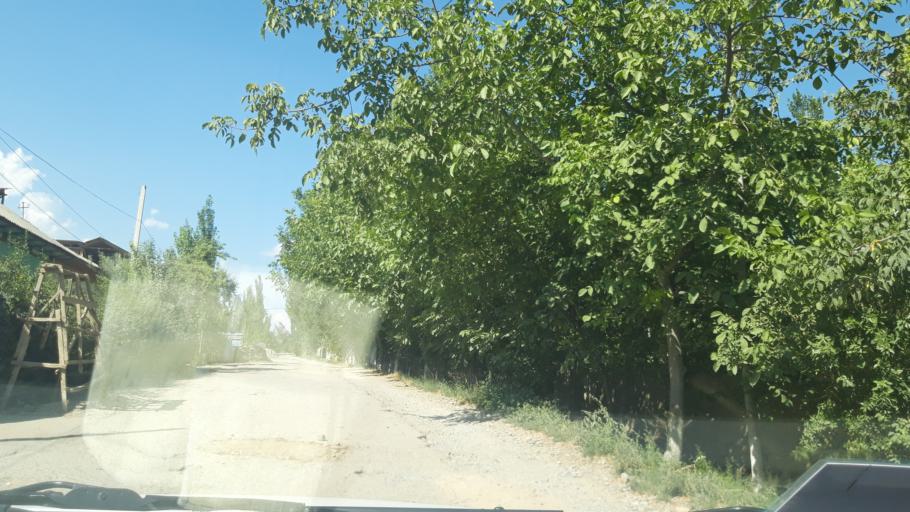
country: UZ
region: Namangan
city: Yangiqo`rg`on
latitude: 41.2148
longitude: 71.7144
